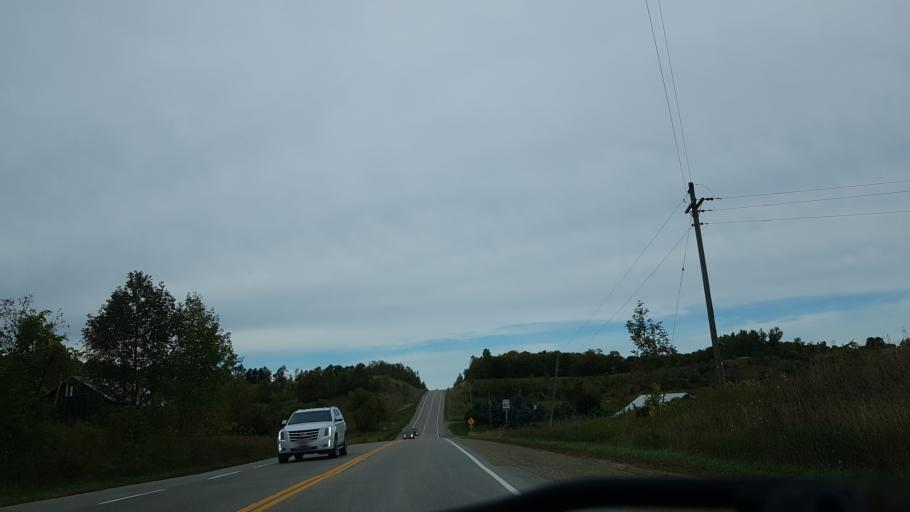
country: CA
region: Ontario
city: Orangeville
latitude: 44.0530
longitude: -80.0120
